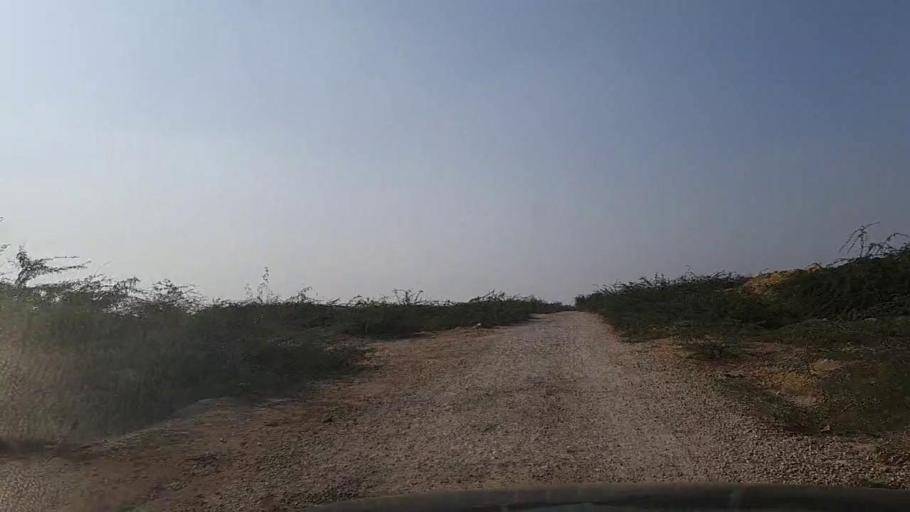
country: PK
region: Sindh
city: Gharo
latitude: 24.7533
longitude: 67.5379
